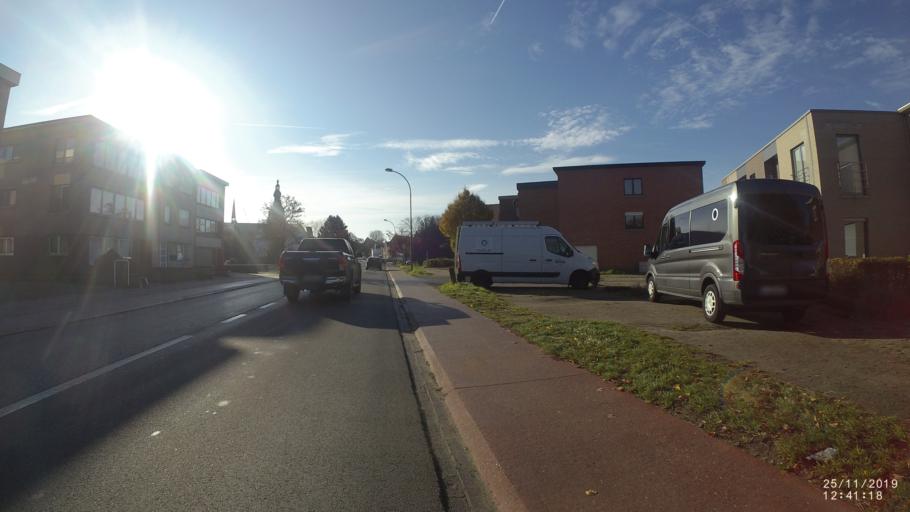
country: BE
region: Flanders
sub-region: Provincie Vlaams-Brabant
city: Aarschot
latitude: 50.9886
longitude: 4.8341
